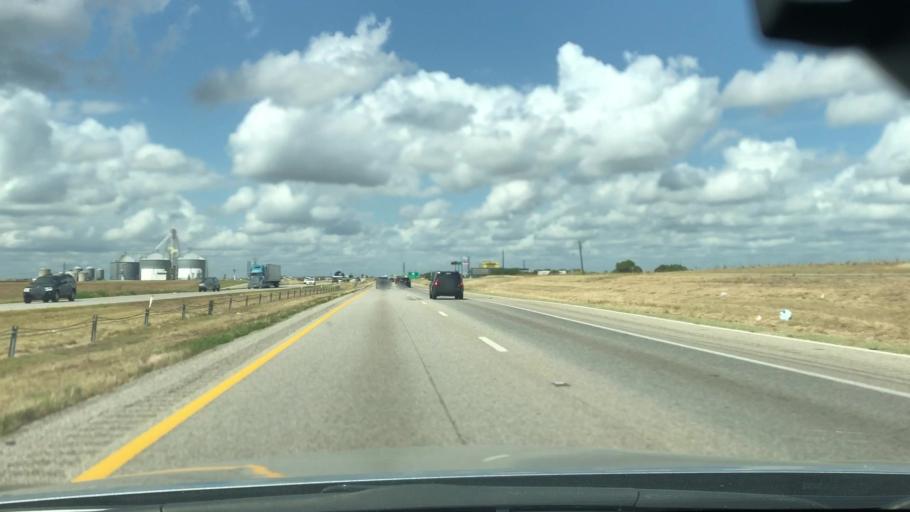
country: US
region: Texas
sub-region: Guadalupe County
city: McQueeney
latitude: 29.5431
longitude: -98.0644
